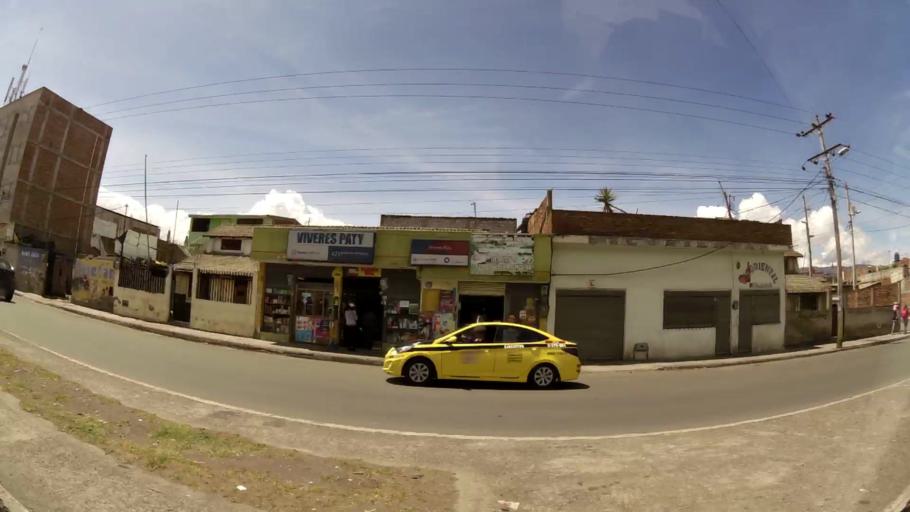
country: EC
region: Chimborazo
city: Riobamba
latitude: -1.6625
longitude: -78.6392
